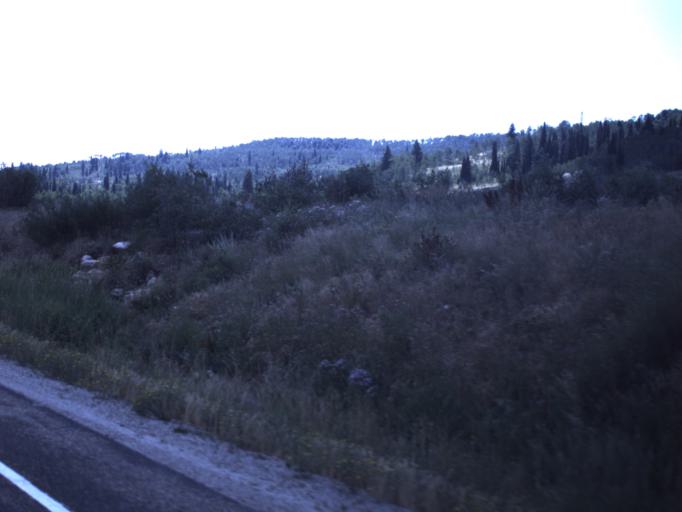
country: US
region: Utah
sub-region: Cache County
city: Richmond
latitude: 41.8913
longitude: -111.5657
